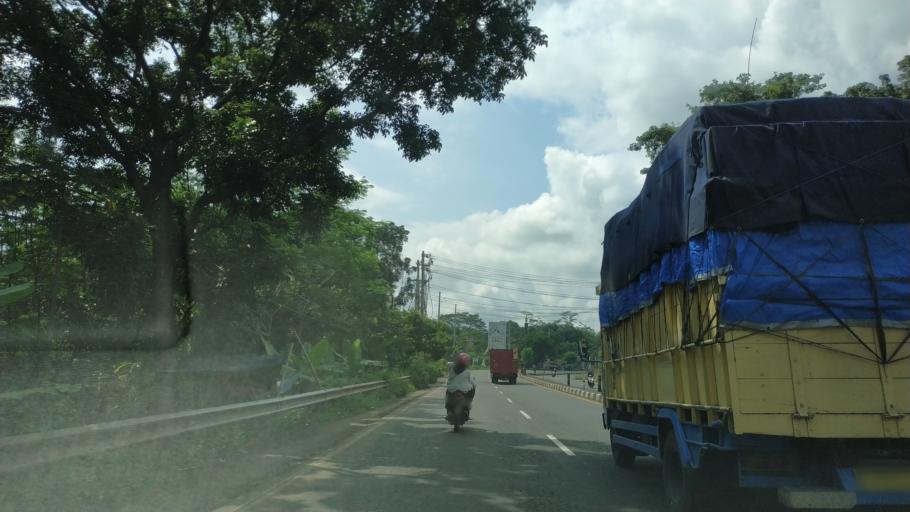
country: ID
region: Central Java
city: Pekalongan
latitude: -6.9332
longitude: 109.7710
